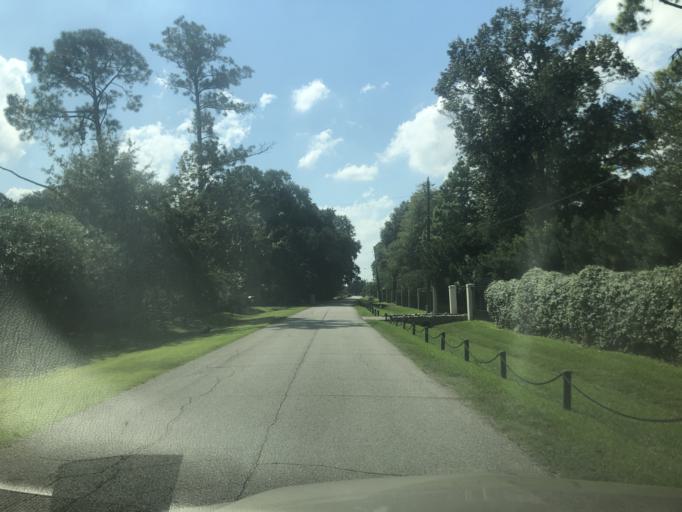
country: US
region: Texas
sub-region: Harris County
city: Bunker Hill Village
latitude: 29.7412
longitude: -95.5457
